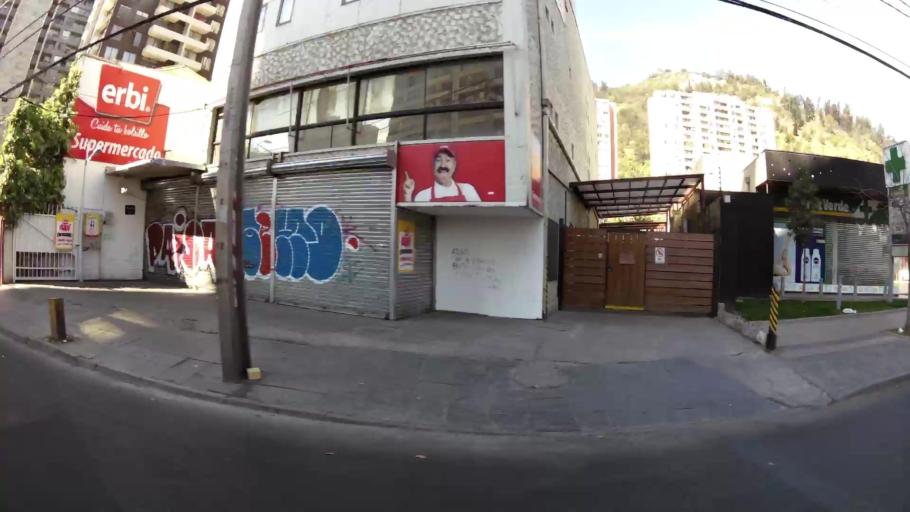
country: CL
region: Santiago Metropolitan
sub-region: Provincia de Santiago
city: Santiago
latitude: -33.4234
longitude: -70.6400
